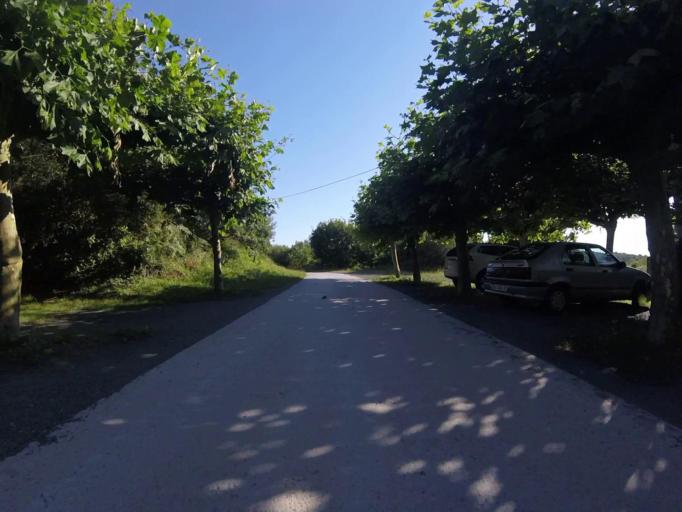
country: ES
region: Basque Country
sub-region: Provincia de Guipuzcoa
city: Fuenterrabia
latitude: 43.3844
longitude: -1.7996
